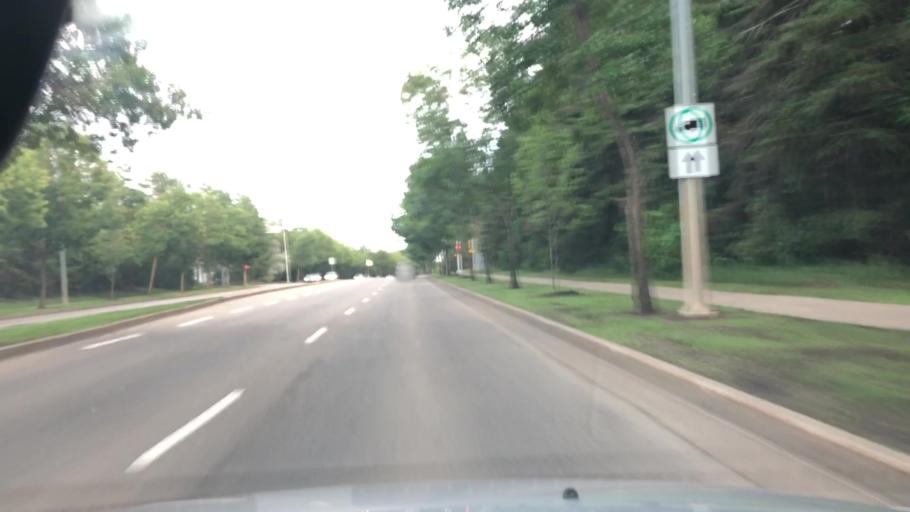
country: CA
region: Alberta
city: St. Albert
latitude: 53.6391
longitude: -113.5955
